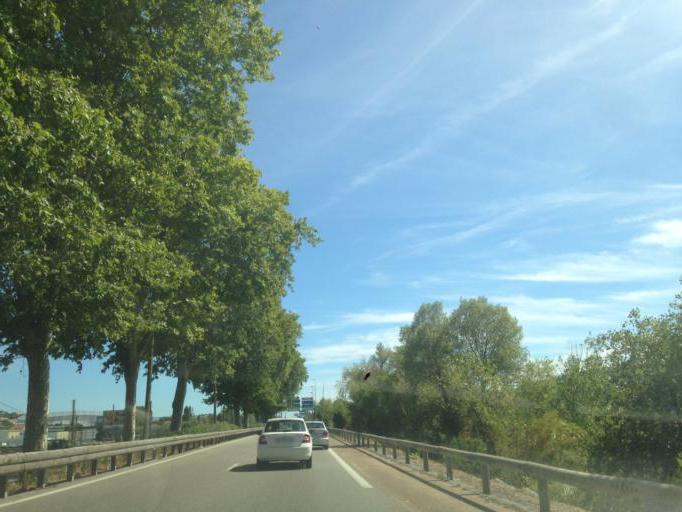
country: FR
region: Provence-Alpes-Cote d'Azur
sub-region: Departement des Alpes-Maritimes
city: La Gaude
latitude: 43.7148
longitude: 7.1870
